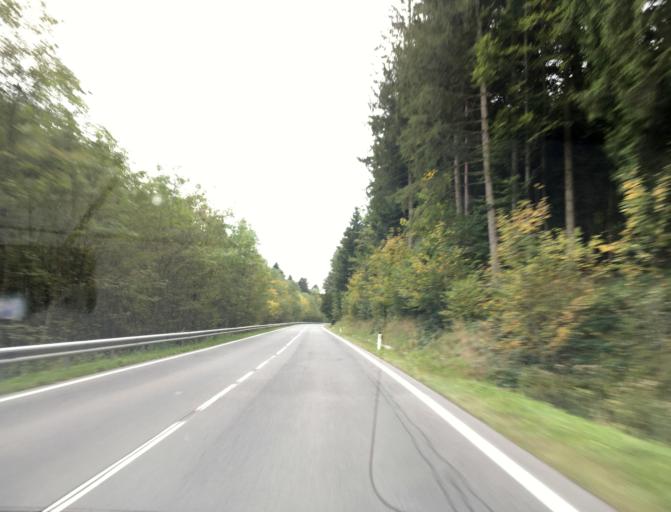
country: AT
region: Lower Austria
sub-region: Politischer Bezirk Neunkirchen
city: Thomasberg
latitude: 47.5560
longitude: 16.1423
